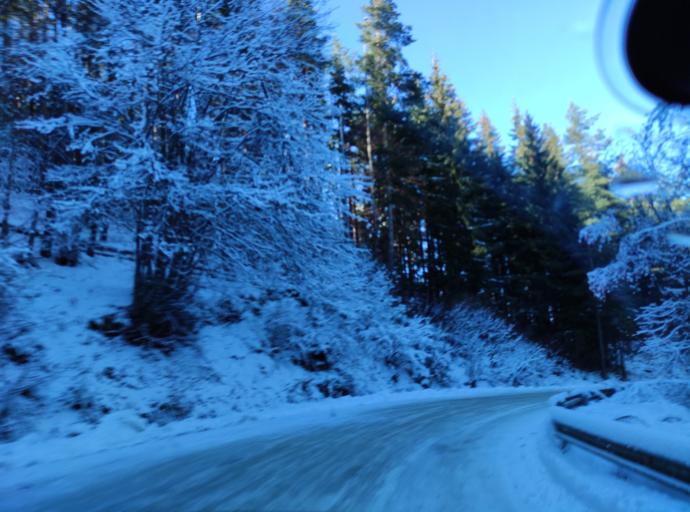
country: BG
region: Sofia-Capital
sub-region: Stolichna Obshtina
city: Sofia
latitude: 42.5998
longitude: 23.3032
